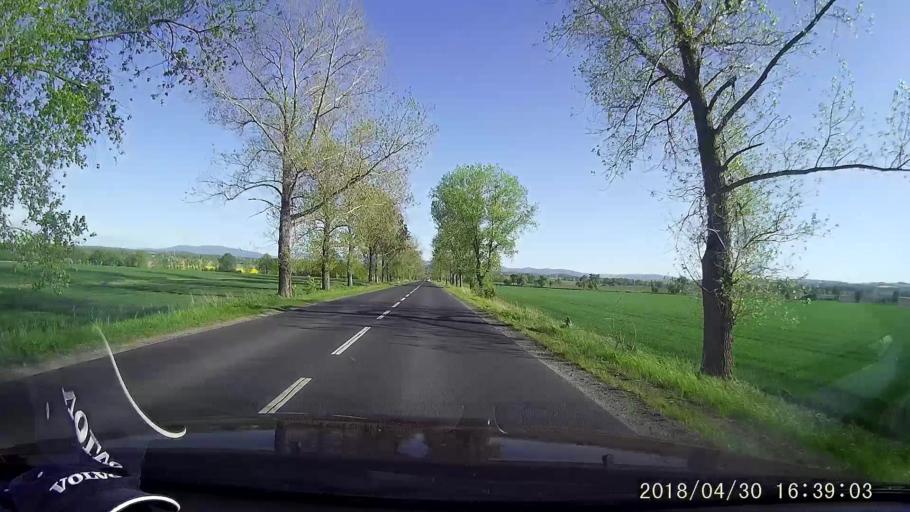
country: PL
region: Silesian Voivodeship
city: Zawidow
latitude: 51.0462
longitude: 15.0437
